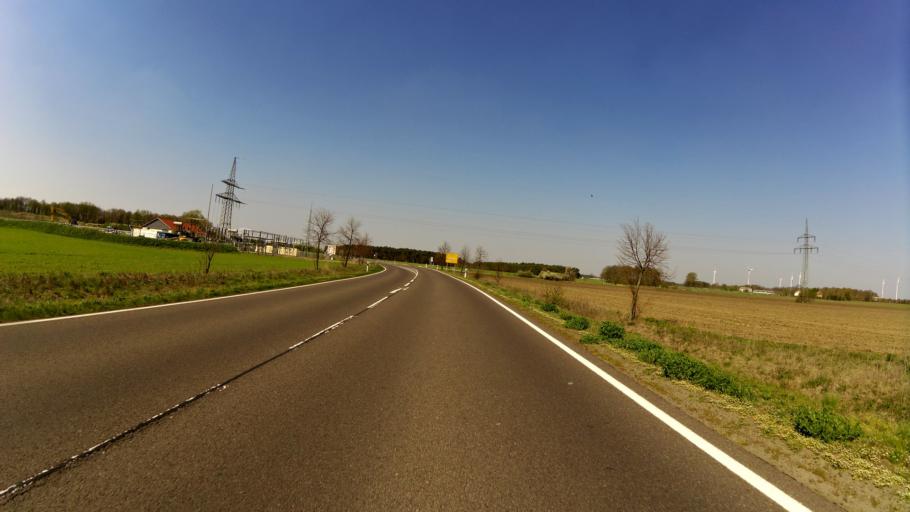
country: DE
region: Saxony-Anhalt
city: Mieste
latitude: 52.4909
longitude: 11.2091
